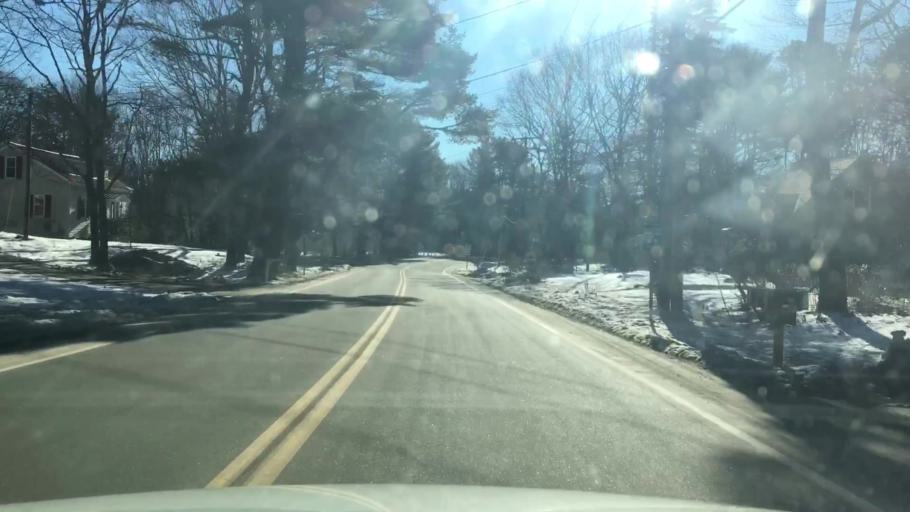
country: US
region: Maine
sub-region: Cumberland County
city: Brunswick
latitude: 43.8816
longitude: -69.9682
